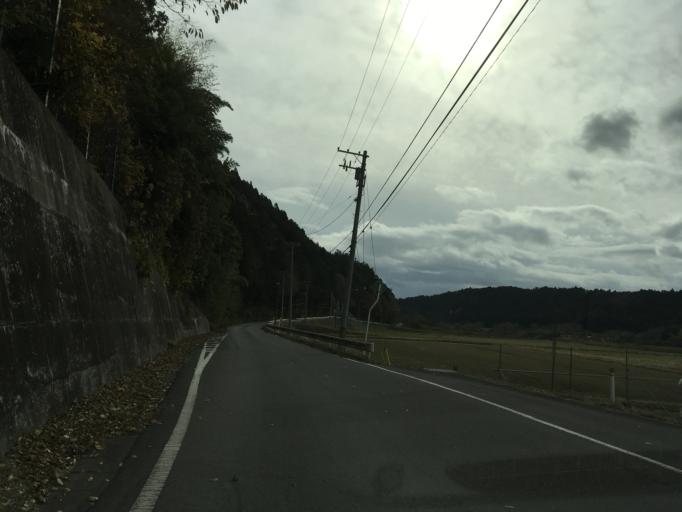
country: JP
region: Iwate
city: Ichinoseki
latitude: 38.7798
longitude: 141.2681
